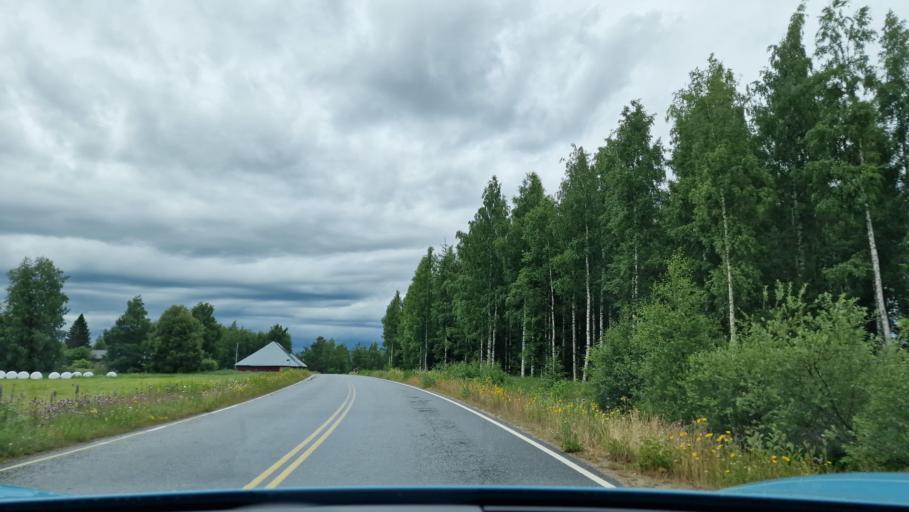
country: FI
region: Central Finland
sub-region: Saarijaervi-Viitasaari
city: Pylkoenmaeki
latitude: 62.6792
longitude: 24.5019
